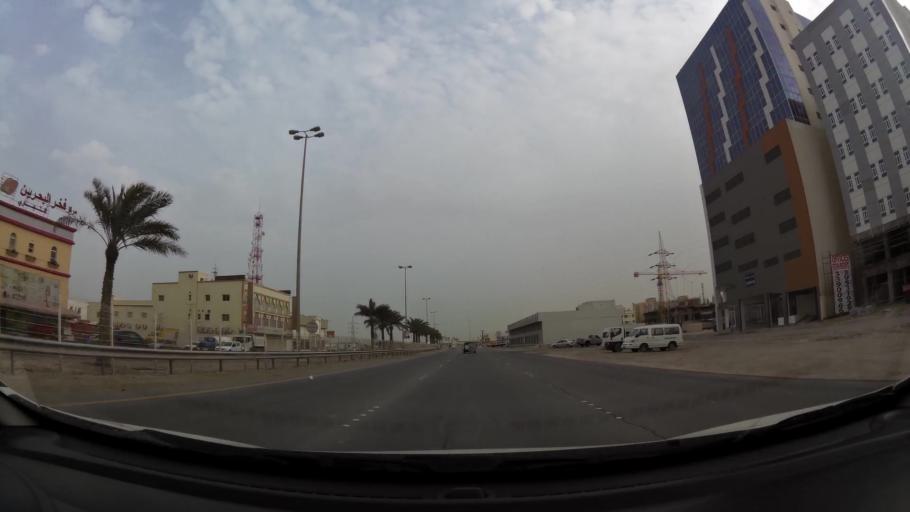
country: BH
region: Northern
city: Ar Rifa'
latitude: 26.1351
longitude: 50.5843
